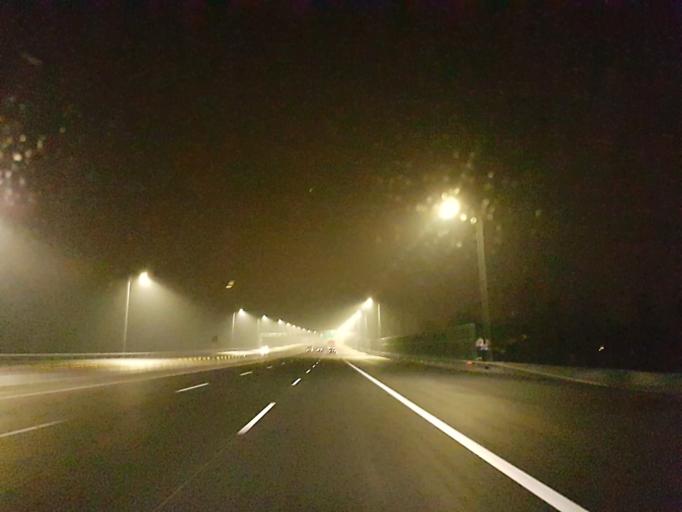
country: PL
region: Masovian Voivodeship
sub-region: Powiat wolominski
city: Marki
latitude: 52.3094
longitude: 21.1144
